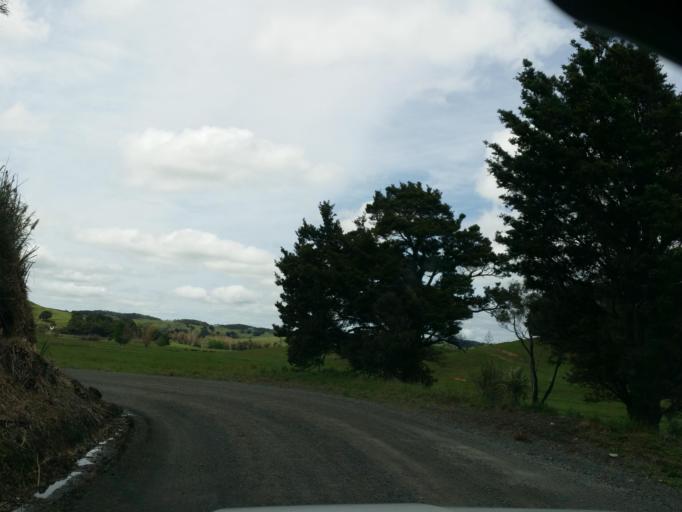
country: NZ
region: Northland
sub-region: Whangarei
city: Maungatapere
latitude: -35.9021
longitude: 174.1487
